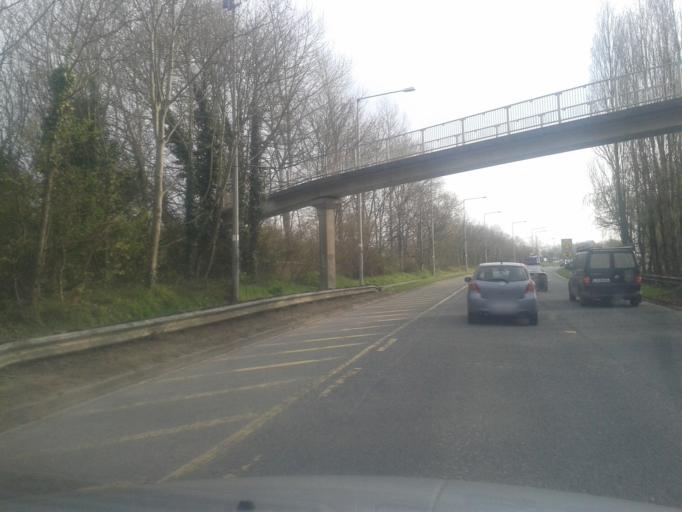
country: IE
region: Leinster
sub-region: Fingal County
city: Swords
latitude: 53.4566
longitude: -6.2127
